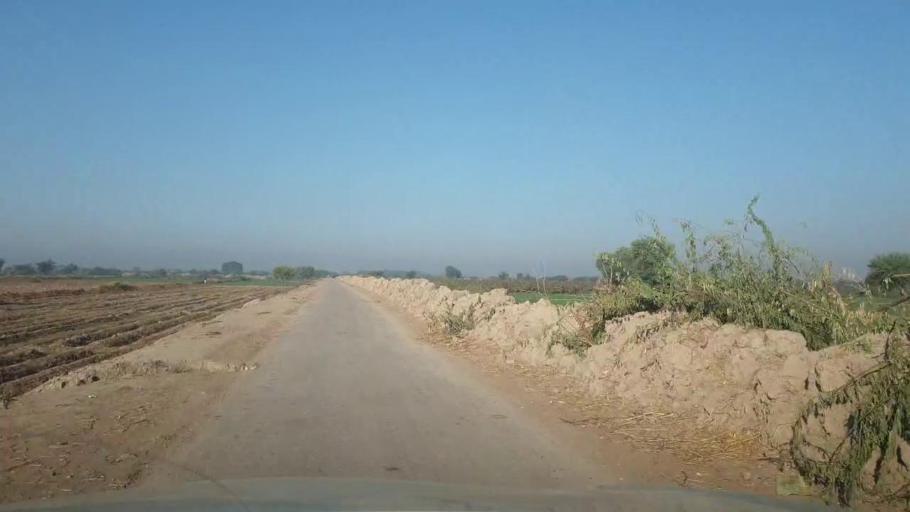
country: PK
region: Sindh
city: Bhan
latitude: 26.5492
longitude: 67.7062
